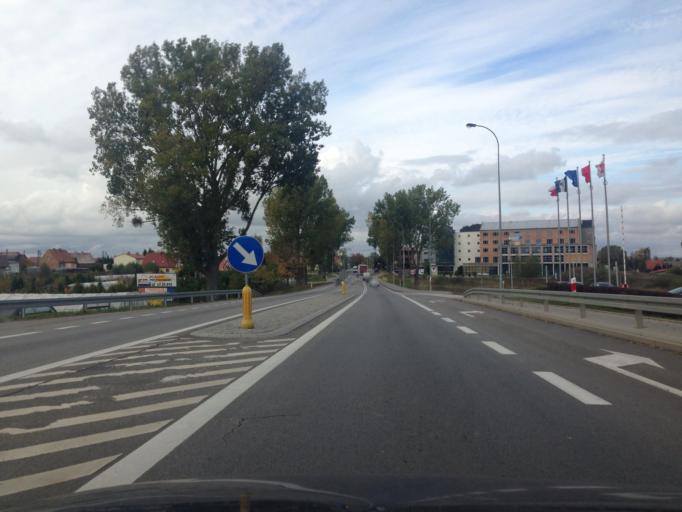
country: PL
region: Pomeranian Voivodeship
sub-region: Powiat gdanski
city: Legowo
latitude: 54.2154
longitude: 18.6548
